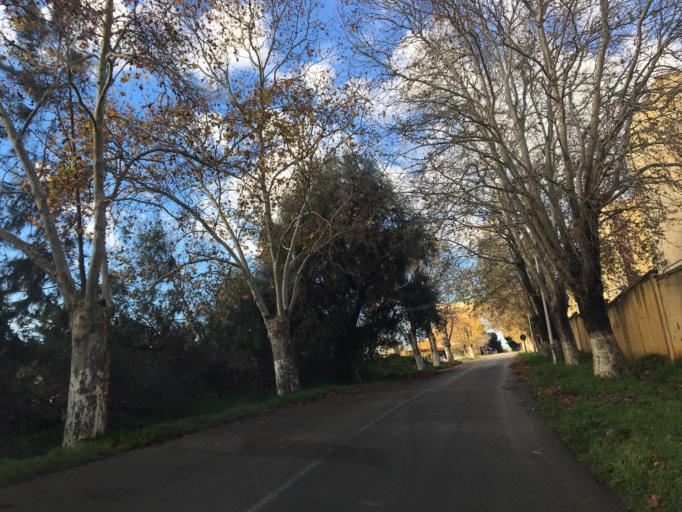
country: DZ
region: Tipaza
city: Tipasa
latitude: 36.5689
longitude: 2.3970
